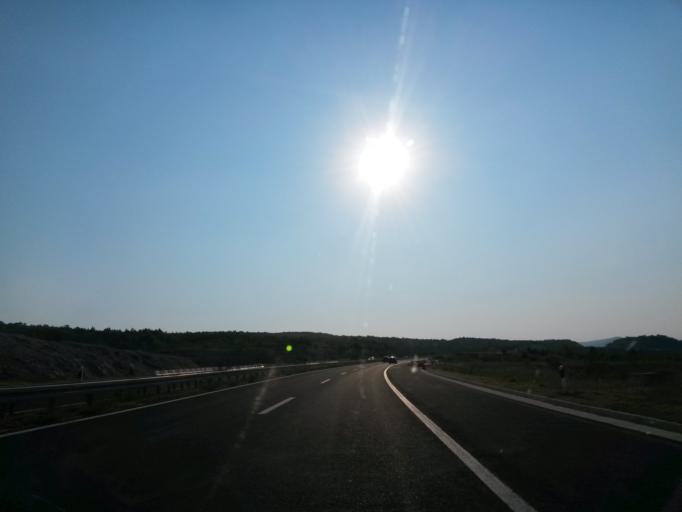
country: HR
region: Splitsko-Dalmatinska
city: Dugopolje
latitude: 43.5821
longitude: 16.6500
